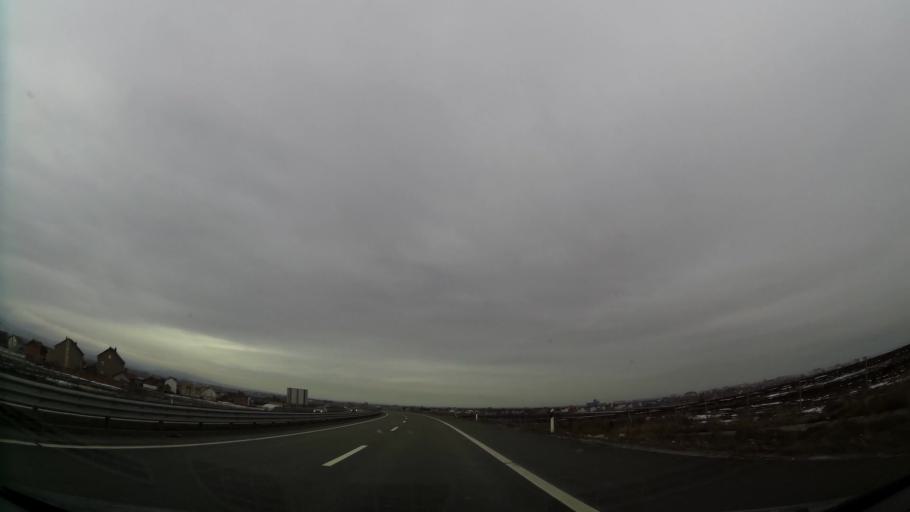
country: XK
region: Pristina
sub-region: Lipjan
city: Lipljan
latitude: 42.5385
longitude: 21.1341
